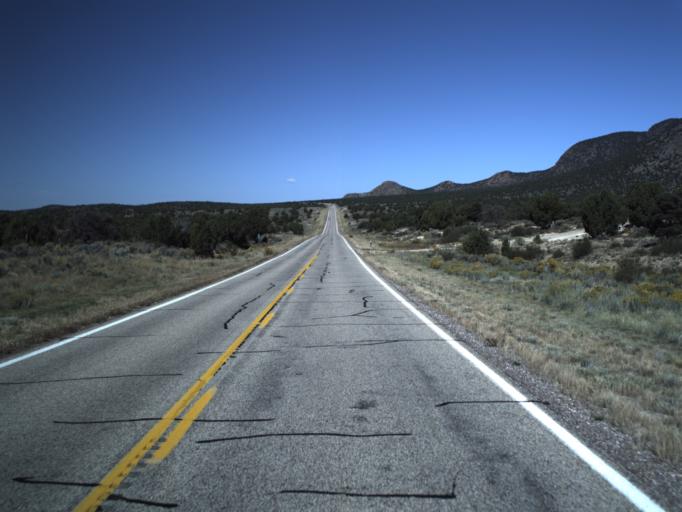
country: US
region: Utah
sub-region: Washington County
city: Enterprise
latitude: 37.6452
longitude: -113.4433
